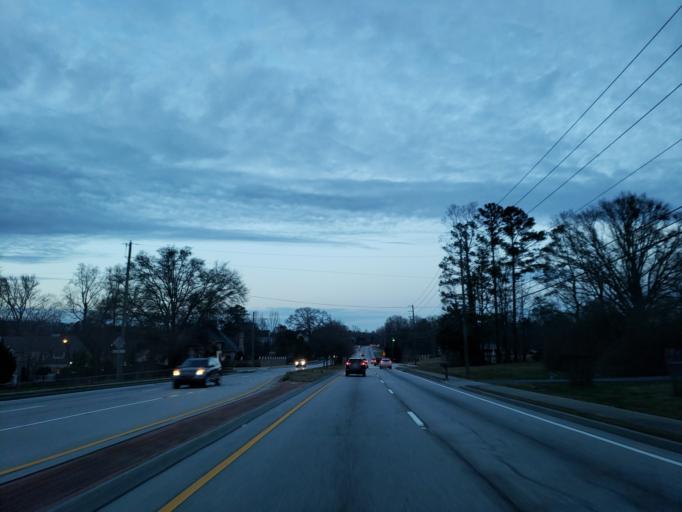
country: US
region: Georgia
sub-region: Cobb County
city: Marietta
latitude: 33.9346
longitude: -84.6298
